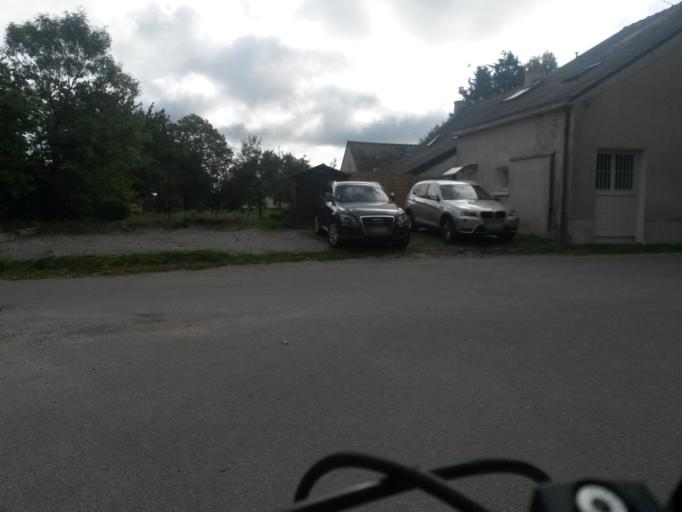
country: FR
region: Pays de la Loire
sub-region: Departement de la Loire-Atlantique
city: Guerande
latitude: 47.3371
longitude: -2.3932
